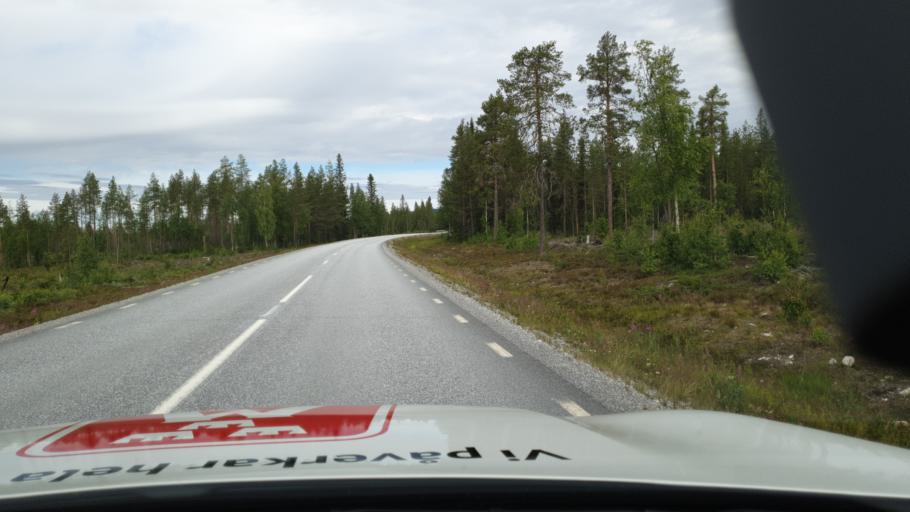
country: SE
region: Vaesterbotten
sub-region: Storumans Kommun
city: Storuman
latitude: 65.2183
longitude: 16.9787
